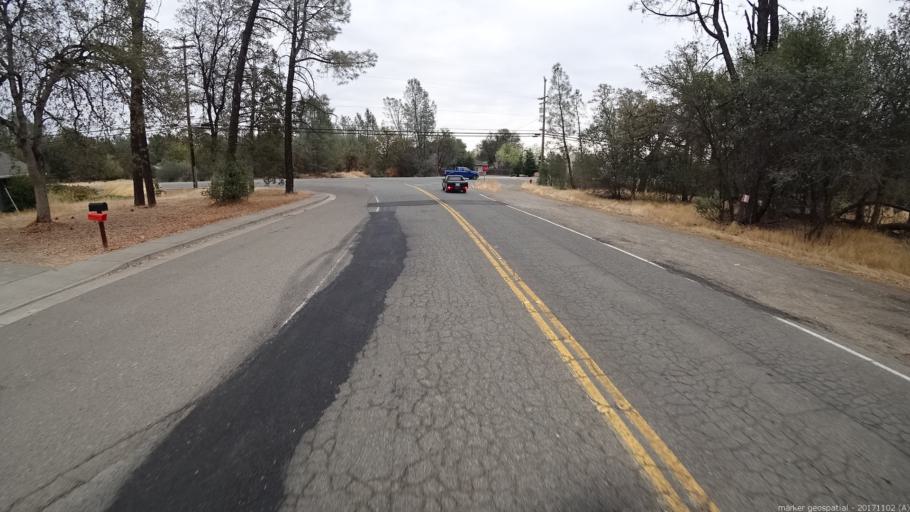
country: US
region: California
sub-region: Shasta County
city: Redding
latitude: 40.6321
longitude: -122.4056
